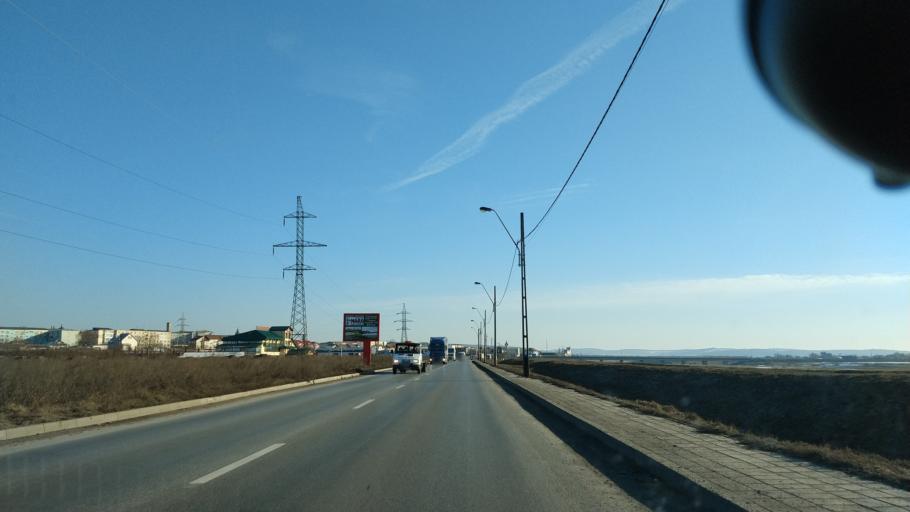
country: RO
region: Neamt
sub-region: Municipiul Roman
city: Roman
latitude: 46.9217
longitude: 26.9138
